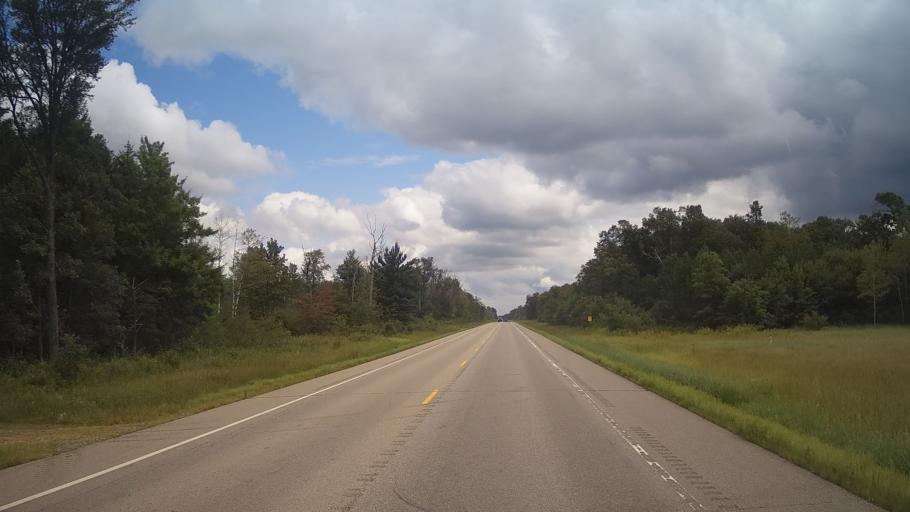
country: US
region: Wisconsin
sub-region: Adams County
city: Friendship
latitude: 44.0253
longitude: -89.7342
